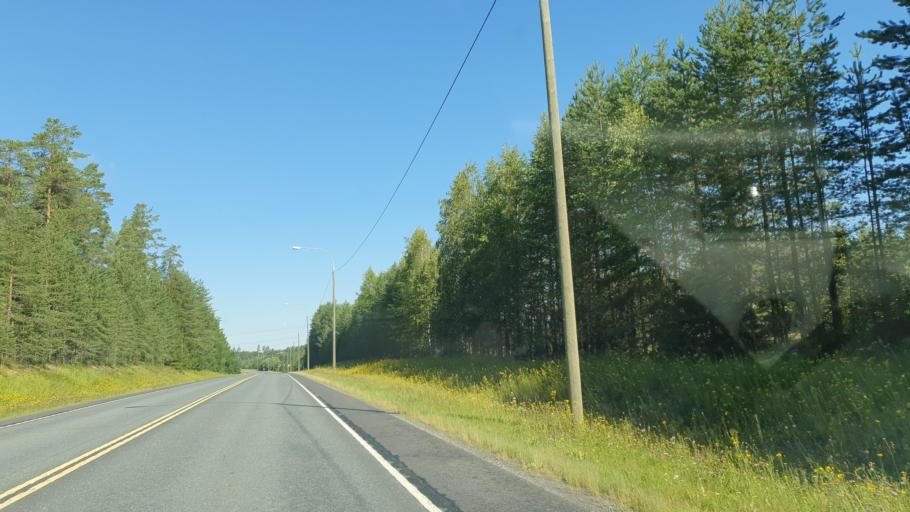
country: FI
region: Northern Savo
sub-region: Kuopio
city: Siilinjaervi
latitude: 63.1813
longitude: 27.5508
